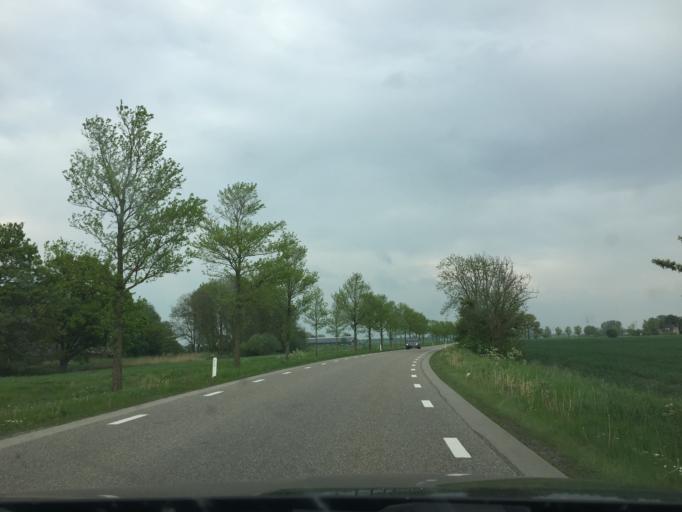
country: NL
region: Groningen
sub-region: Gemeente Zuidhorn
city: Aduard
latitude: 53.2659
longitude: 6.4487
